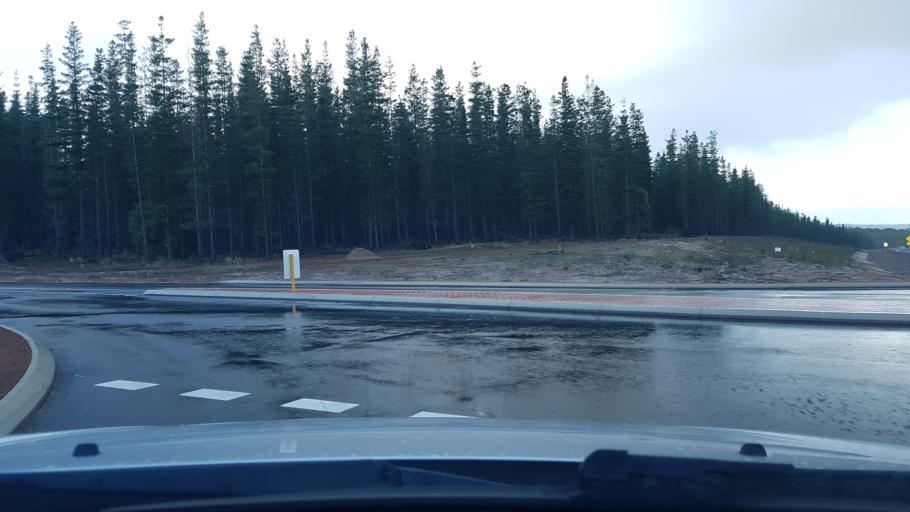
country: AU
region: Western Australia
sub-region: Augusta-Margaret River Shire
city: Margaret River
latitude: -33.9358
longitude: 115.0892
